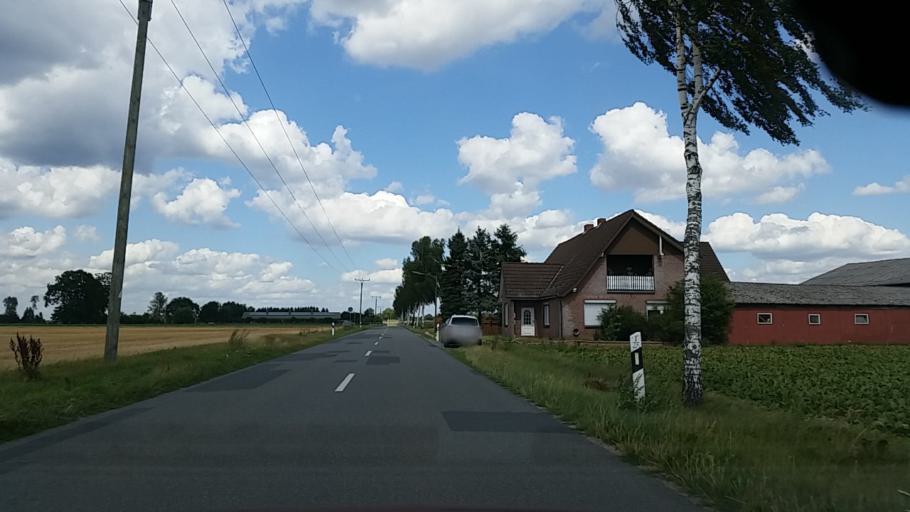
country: DE
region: Lower Saxony
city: Sprakensehl
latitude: 52.7377
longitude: 10.5135
